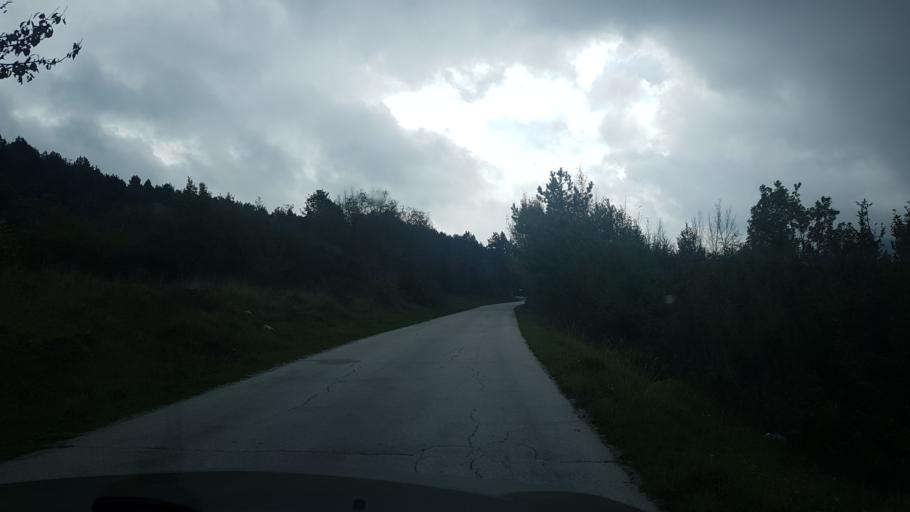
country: HR
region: Istarska
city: Buzet
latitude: 45.5025
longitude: 13.9926
